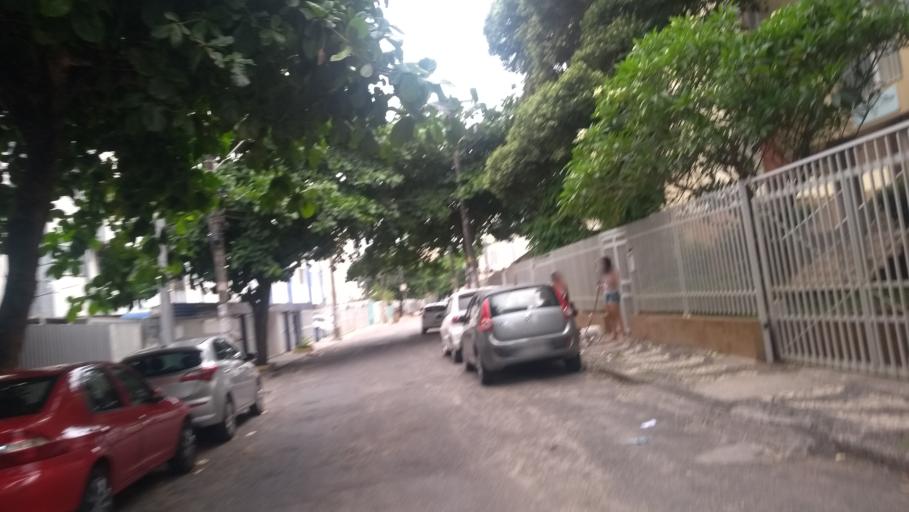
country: BR
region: Bahia
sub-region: Salvador
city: Salvador
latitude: -12.9946
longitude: -38.4468
